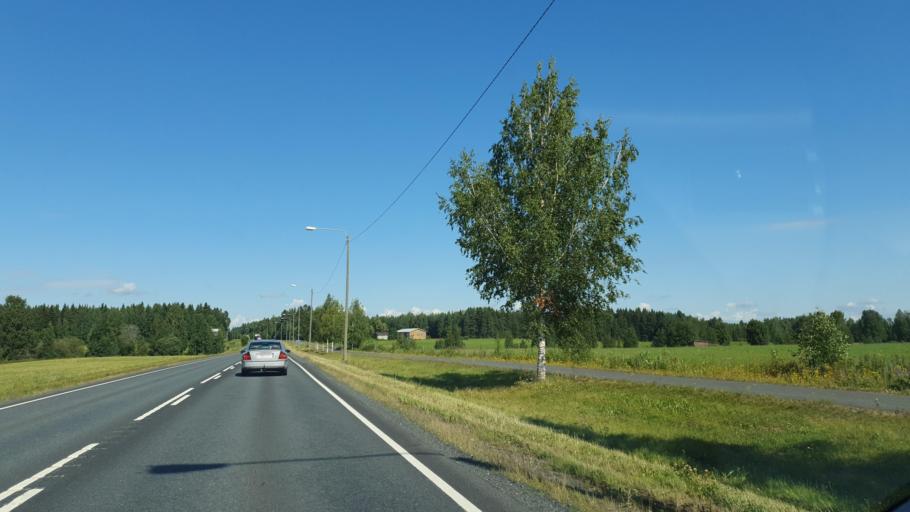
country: FI
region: Northern Savo
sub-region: Ylae-Savo
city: Lapinlahti
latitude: 63.4353
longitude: 27.3264
